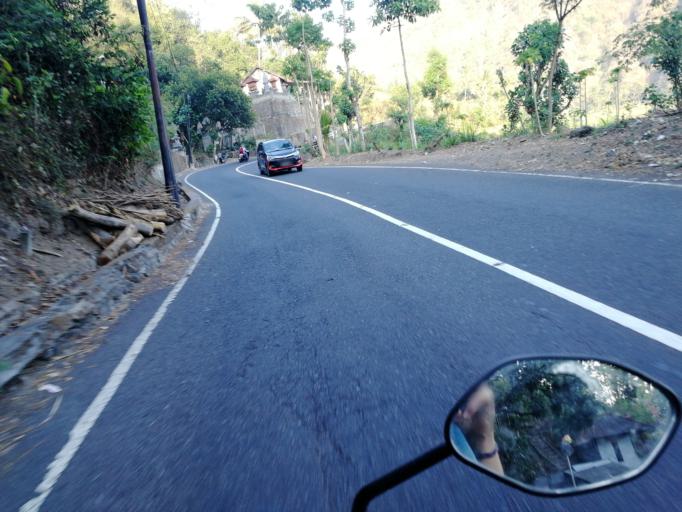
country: ID
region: Bali
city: Banjar Kangkaang
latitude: -8.3675
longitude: 115.6134
